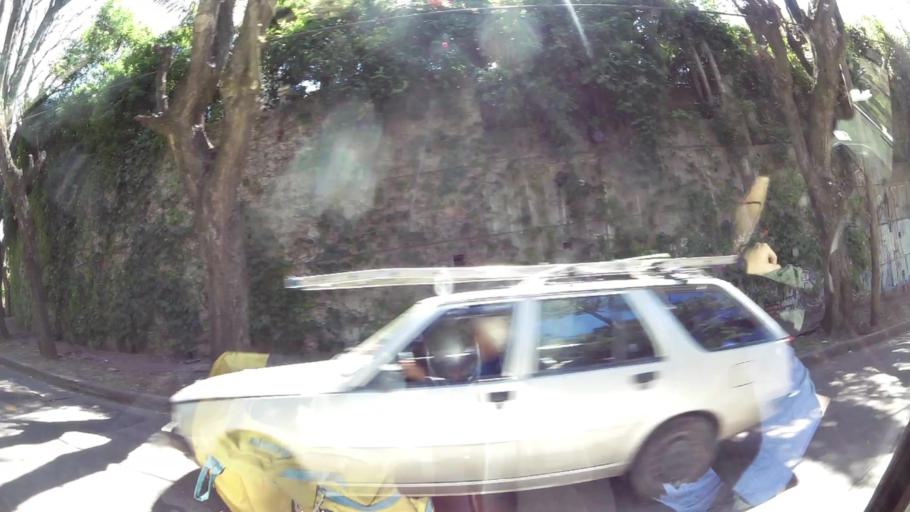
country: AR
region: Buenos Aires
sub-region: Partido de San Isidro
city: San Isidro
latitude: -34.4718
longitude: -58.4994
